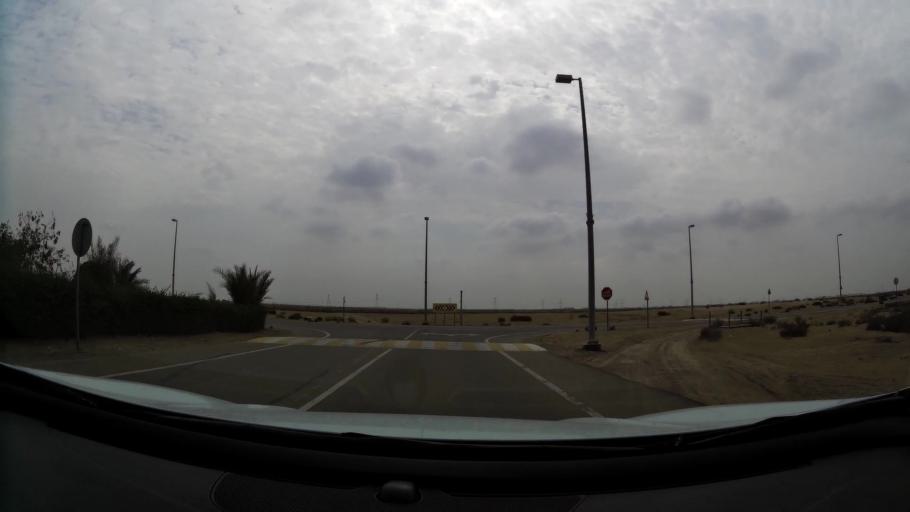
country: AE
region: Abu Dhabi
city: Abu Dhabi
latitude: 24.6515
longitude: 54.6865
